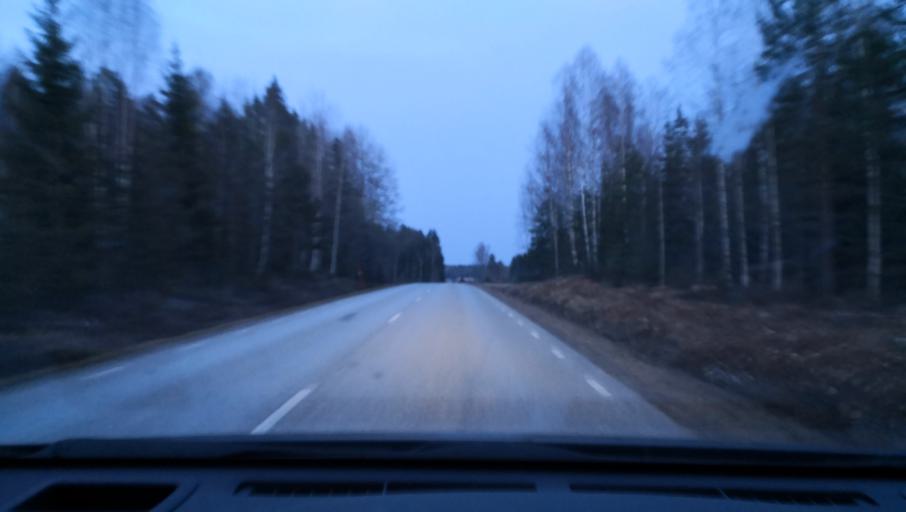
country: SE
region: OErebro
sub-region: Lindesbergs Kommun
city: Lindesberg
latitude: 59.5975
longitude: 15.3333
